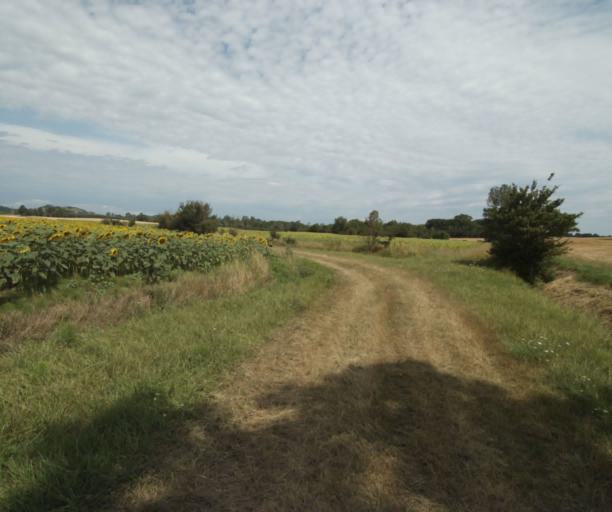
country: FR
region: Midi-Pyrenees
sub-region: Departement de la Haute-Garonne
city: Saint-Felix-Lauragais
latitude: 43.4165
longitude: 1.9197
